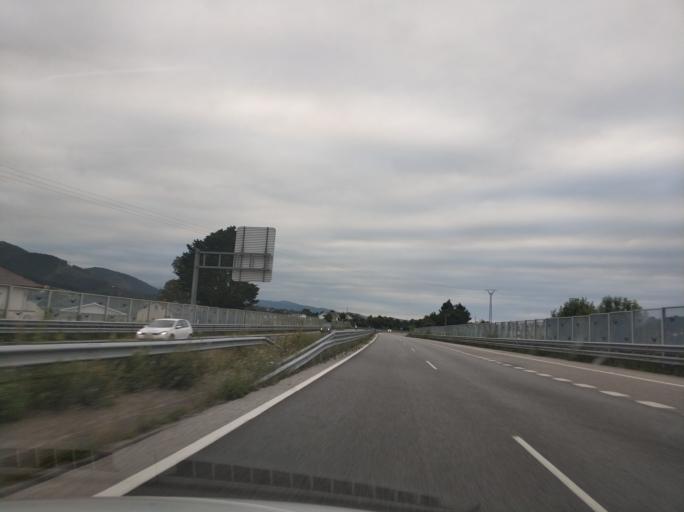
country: ES
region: Asturias
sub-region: Province of Asturias
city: Tineo
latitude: 43.5463
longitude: -6.4512
